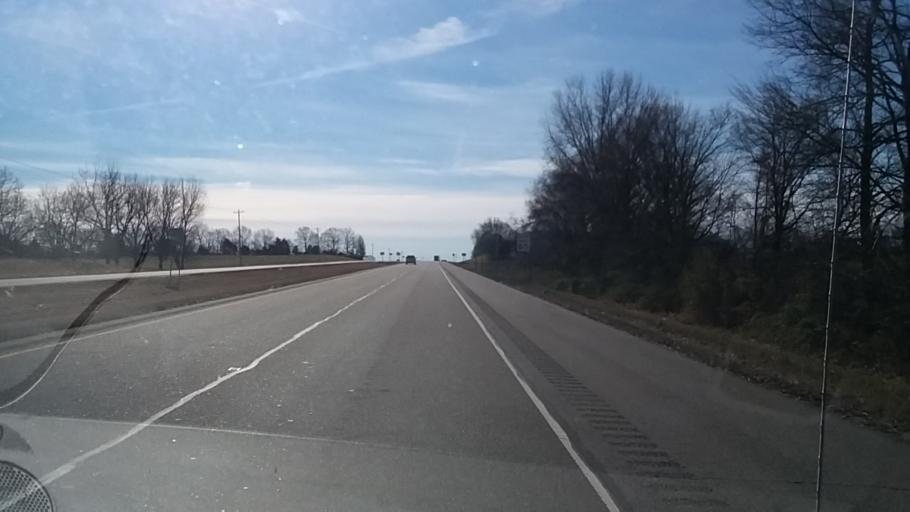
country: US
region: Tennessee
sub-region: Lauderdale County
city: Halls
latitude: 35.8947
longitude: -89.2409
